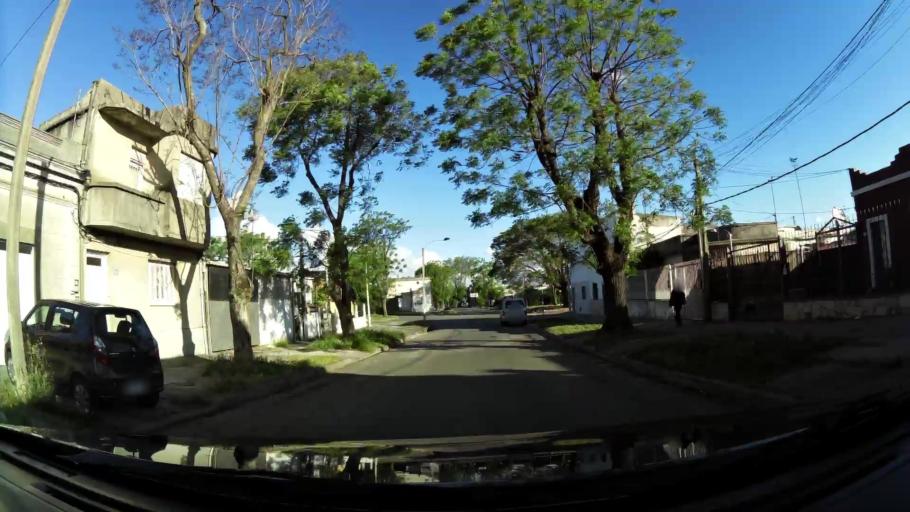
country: UY
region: Montevideo
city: Montevideo
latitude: -34.8742
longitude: -56.1314
